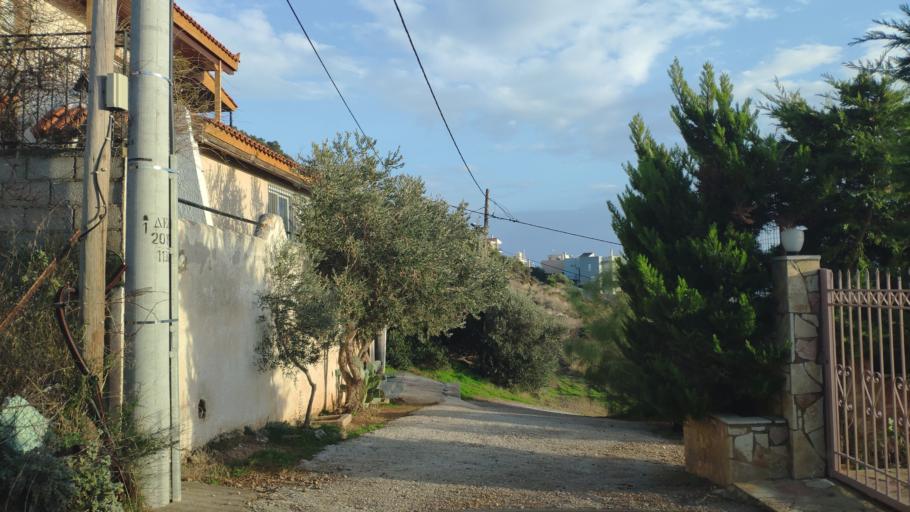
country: GR
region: Attica
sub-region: Nomarchia Anatolikis Attikis
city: Limin Mesoyaias
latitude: 37.9036
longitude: 24.0262
